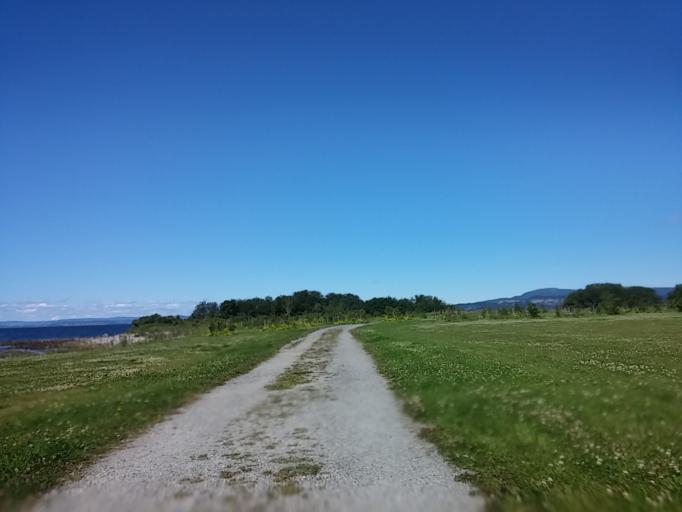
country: NO
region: Sor-Trondelag
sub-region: Malvik
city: Malvik
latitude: 63.4339
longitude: 10.7260
